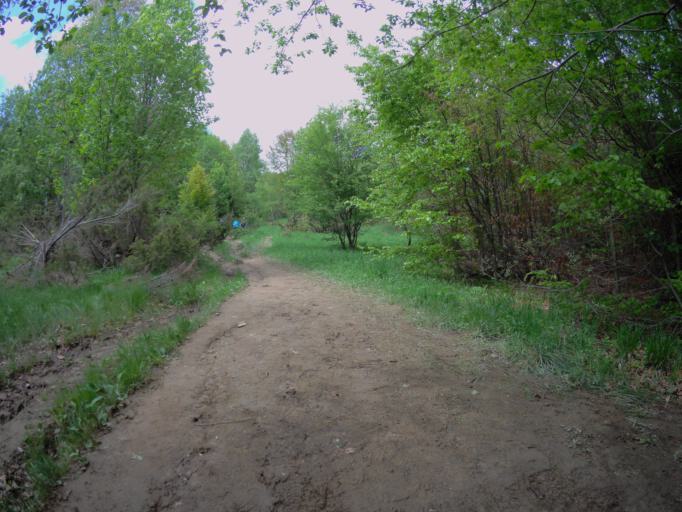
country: PL
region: Subcarpathian Voivodeship
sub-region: Powiat bieszczadzki
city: Lutowiska
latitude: 49.1452
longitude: 22.5627
